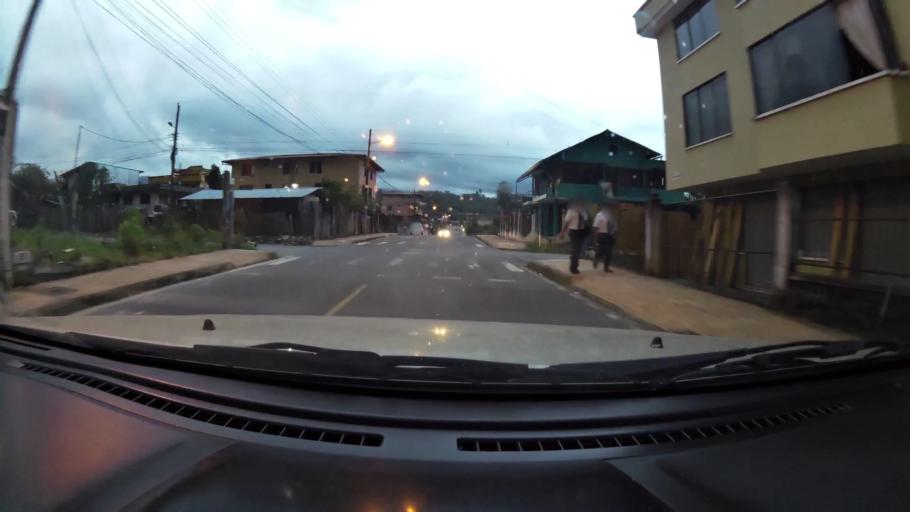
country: EC
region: Pastaza
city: Puyo
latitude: -1.4834
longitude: -78.0067
